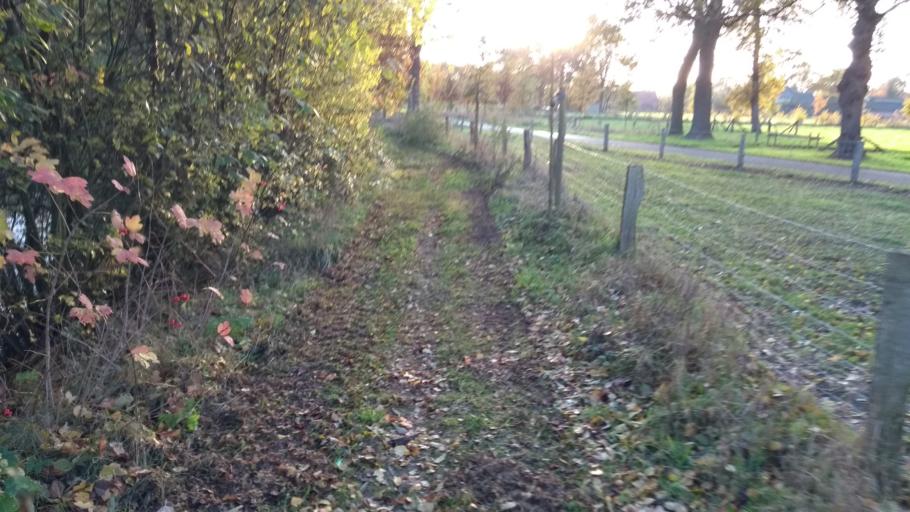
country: NL
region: Overijssel
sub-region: Gemeente Borne
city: Borne
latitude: 52.3303
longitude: 6.7439
